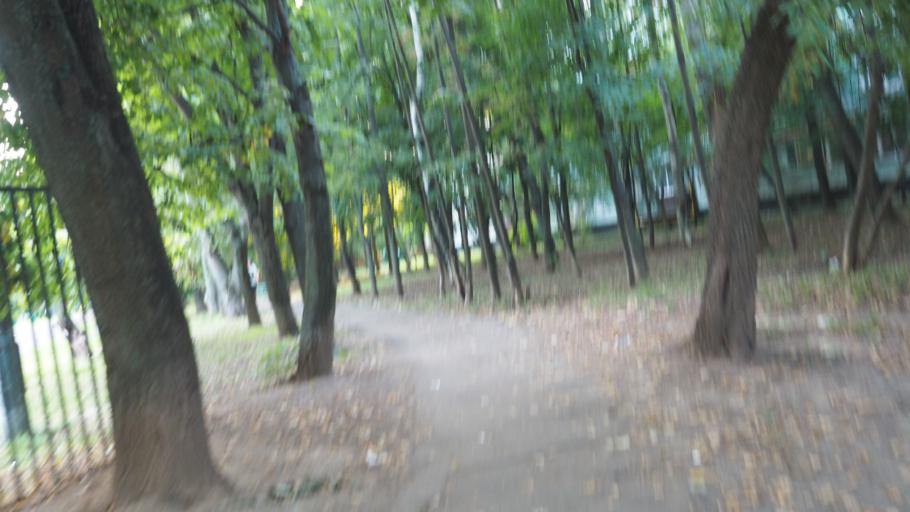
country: RU
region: Moscow
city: Orekhovo-Borisovo
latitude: 55.6018
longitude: 37.7136
